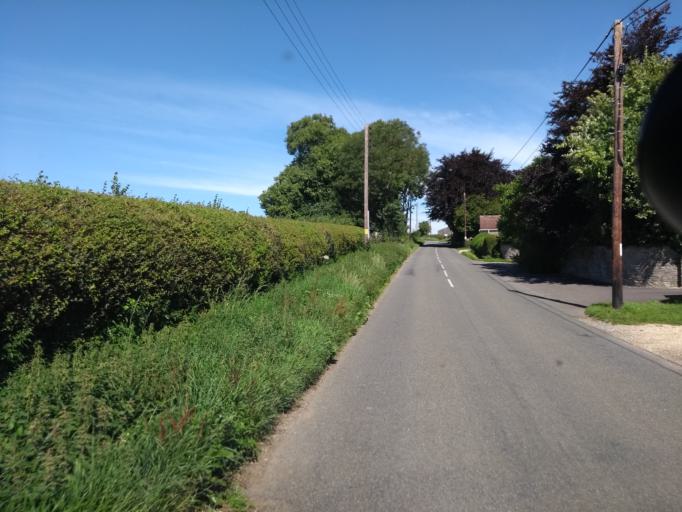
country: GB
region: England
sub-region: Somerset
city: Ilchester
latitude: 51.0616
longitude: -2.6762
